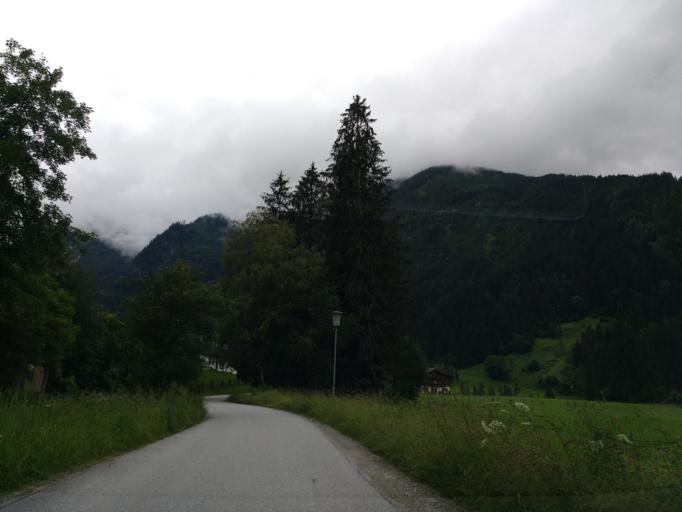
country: AT
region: Salzburg
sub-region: Politischer Bezirk Zell am See
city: Wald im Pinzgau
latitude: 47.2338
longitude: 12.2507
